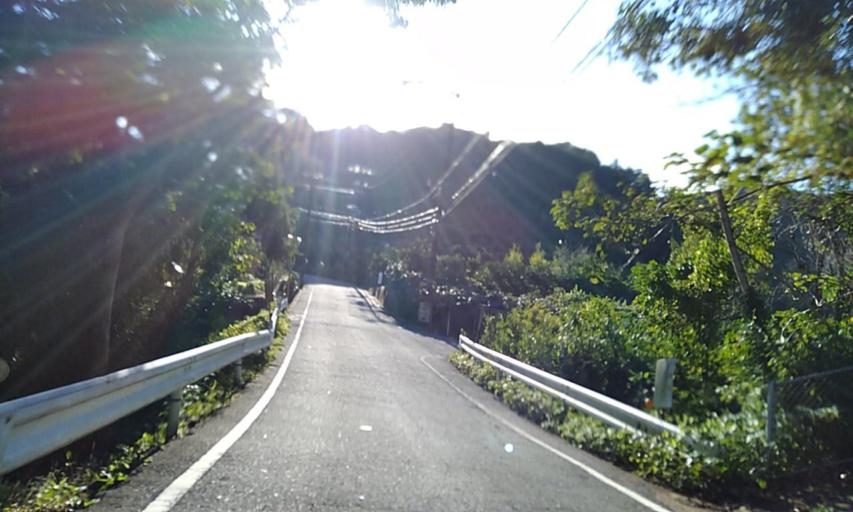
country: JP
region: Wakayama
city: Iwade
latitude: 34.1546
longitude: 135.3061
